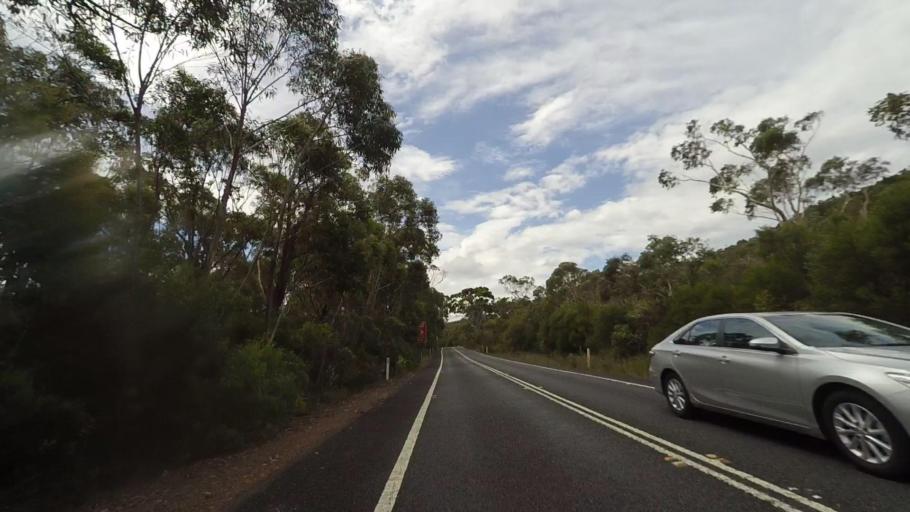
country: AU
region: New South Wales
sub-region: Sutherland Shire
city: Grays Point
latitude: -34.1168
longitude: 151.0695
